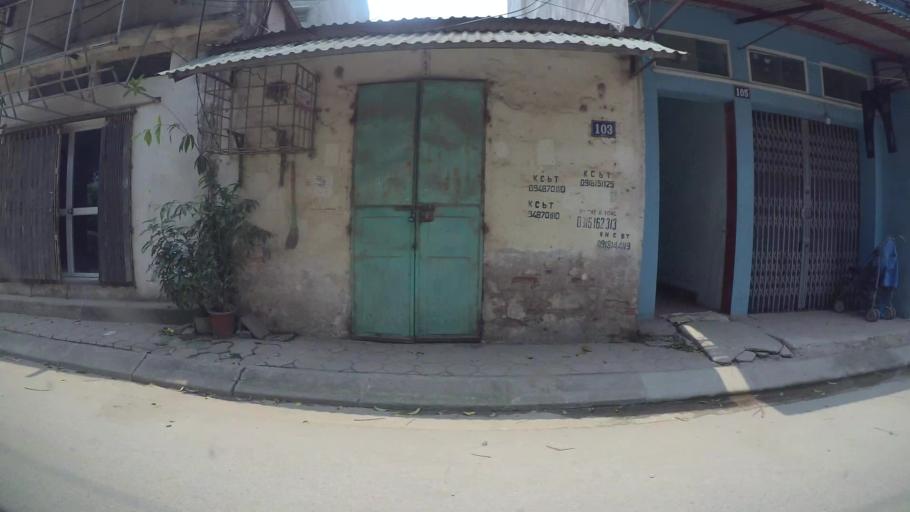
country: VN
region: Ha Noi
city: Ha Dong
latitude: 20.9945
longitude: 105.7733
